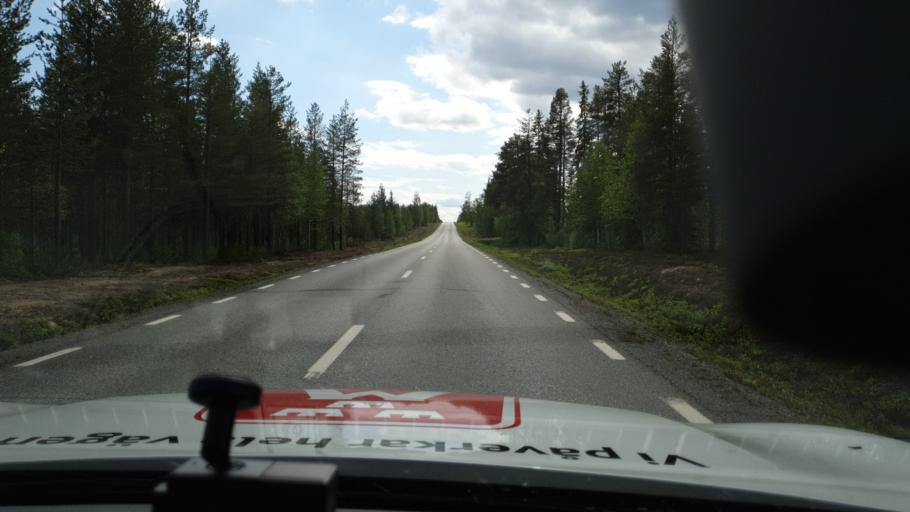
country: SE
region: Vaesterbotten
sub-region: Sorsele Kommun
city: Sorsele
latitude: 65.2330
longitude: 17.6555
